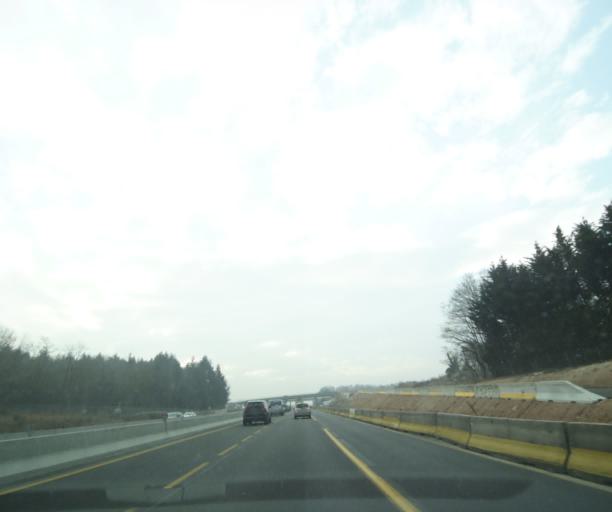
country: FR
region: Rhone-Alpes
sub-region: Departement du Rhone
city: Limonest
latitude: 45.8413
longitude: 4.7521
